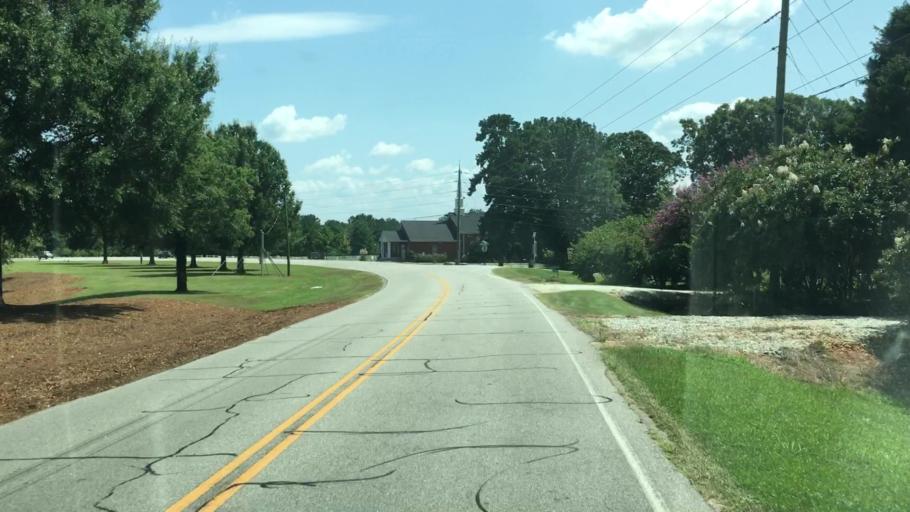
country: US
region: Georgia
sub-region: Oconee County
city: Watkinsville
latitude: 33.8608
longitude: -83.4582
